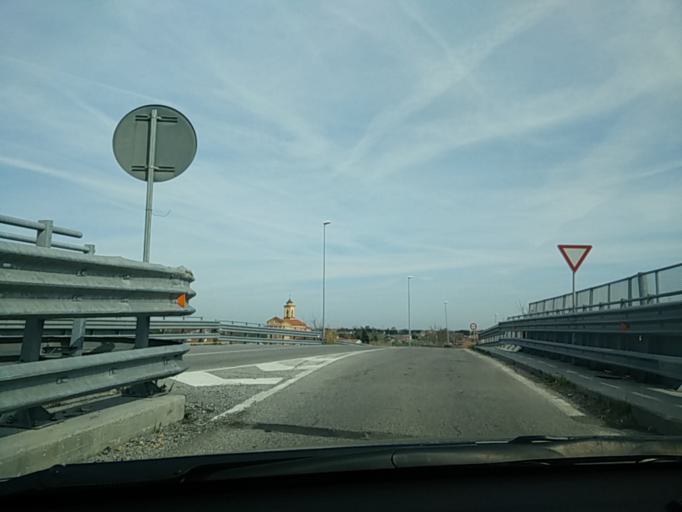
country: IT
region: Emilia-Romagna
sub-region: Provincia di Rimini
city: Santa Giustina
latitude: 44.0705
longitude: 12.5136
